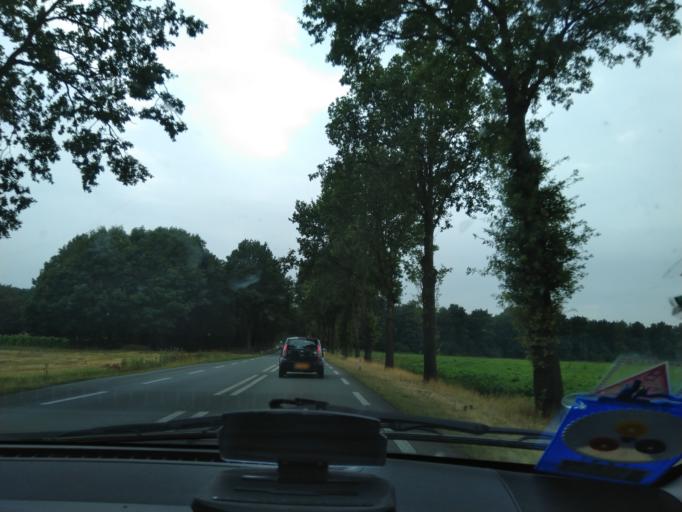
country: NL
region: Groningen
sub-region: Gemeente Pekela
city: Oude Pekela
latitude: 53.1063
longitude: 6.9982
